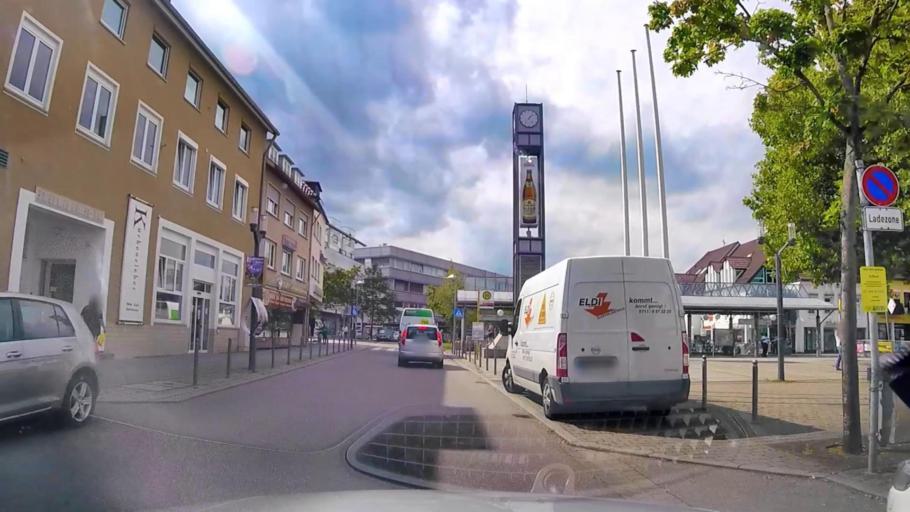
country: DE
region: Baden-Wuerttemberg
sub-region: Regierungsbezirk Stuttgart
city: Korntal
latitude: 48.8138
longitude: 9.1140
